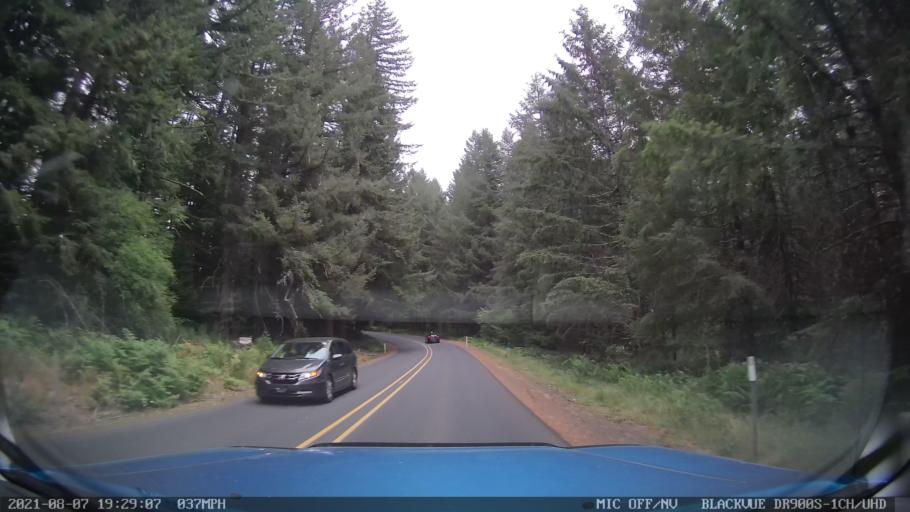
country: US
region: Oregon
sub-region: Linn County
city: Lyons
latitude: 44.8837
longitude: -122.6331
